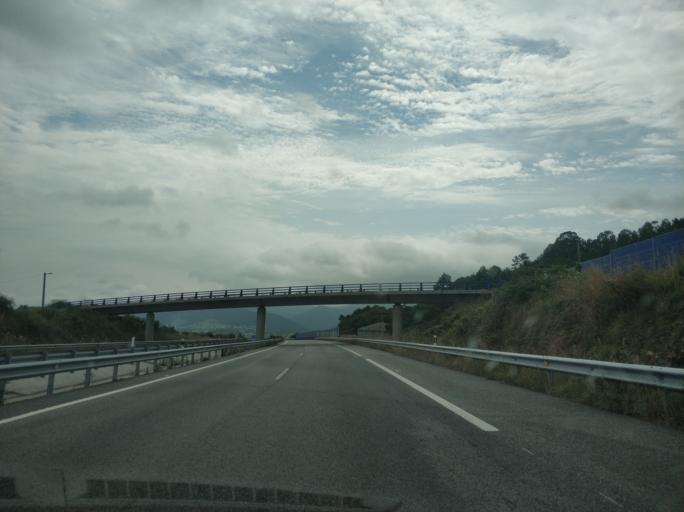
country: ES
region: Asturias
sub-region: Province of Asturias
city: Navia
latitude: 43.5292
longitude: -6.5772
